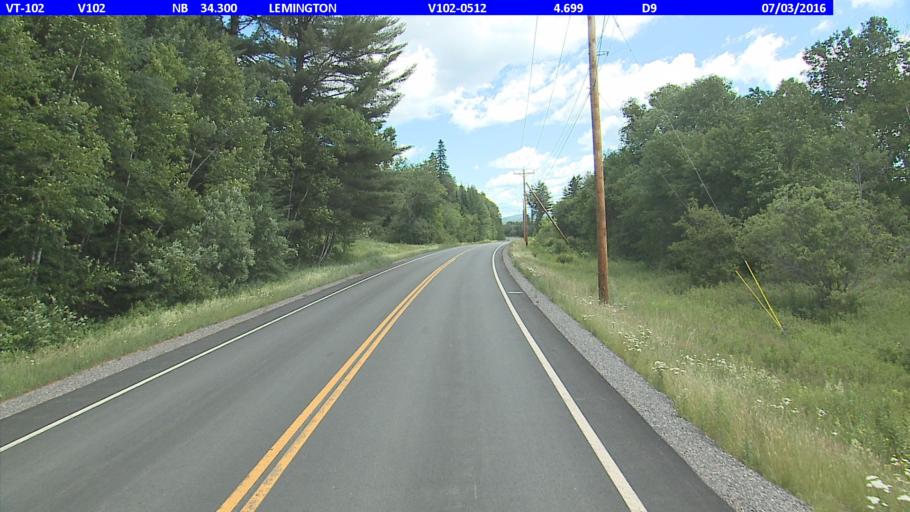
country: US
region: New Hampshire
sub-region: Coos County
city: Colebrook
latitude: 44.8812
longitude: -71.5256
